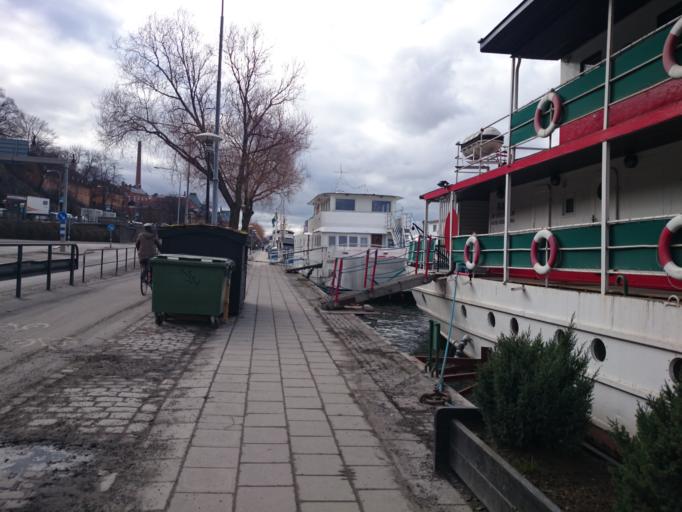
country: SE
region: Stockholm
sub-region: Stockholms Kommun
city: Stockholm
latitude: 59.3214
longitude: 18.0607
